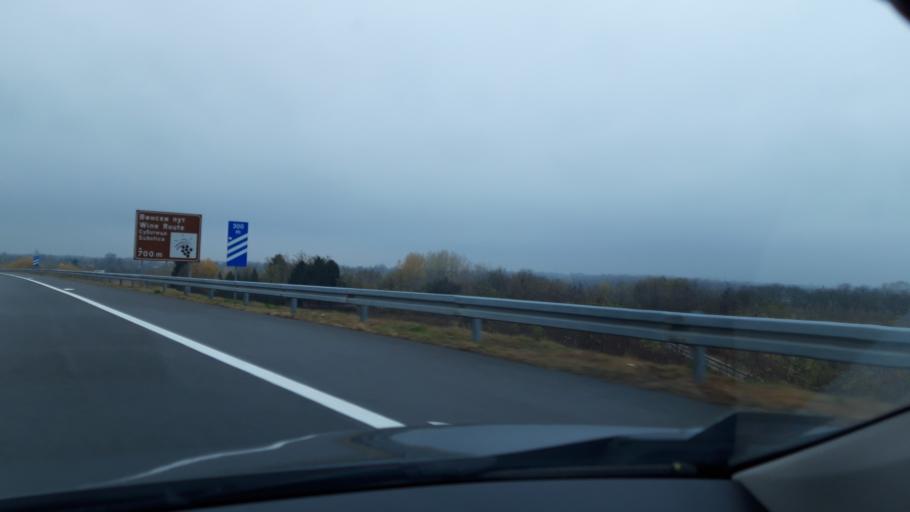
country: HU
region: Csongrad
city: Asotthalom
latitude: 46.1115
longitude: 19.7977
